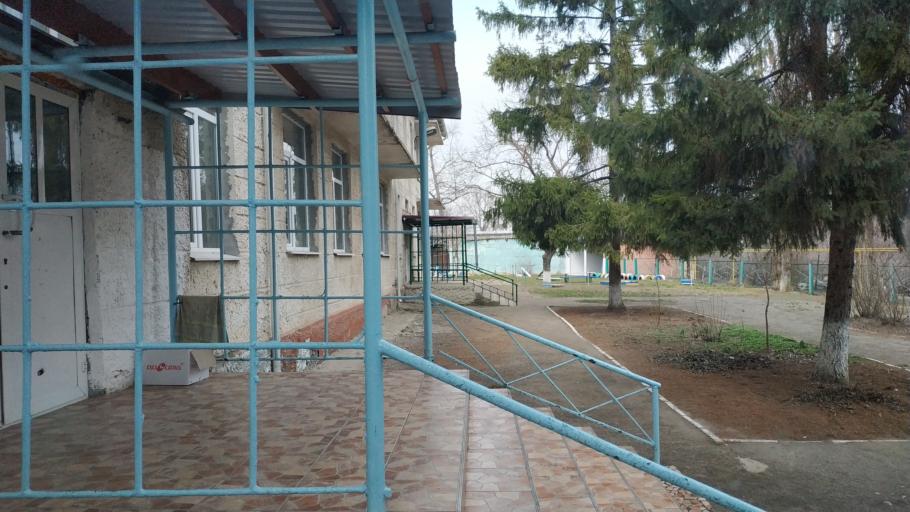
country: MD
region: Chisinau
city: Singera
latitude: 46.9363
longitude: 28.9784
